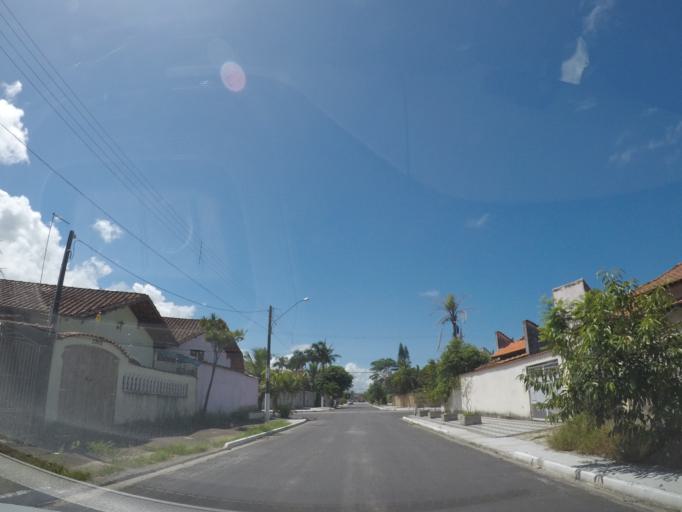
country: BR
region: Sao Paulo
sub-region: Mongagua
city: Mongagua
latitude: -24.0667
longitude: -46.5663
